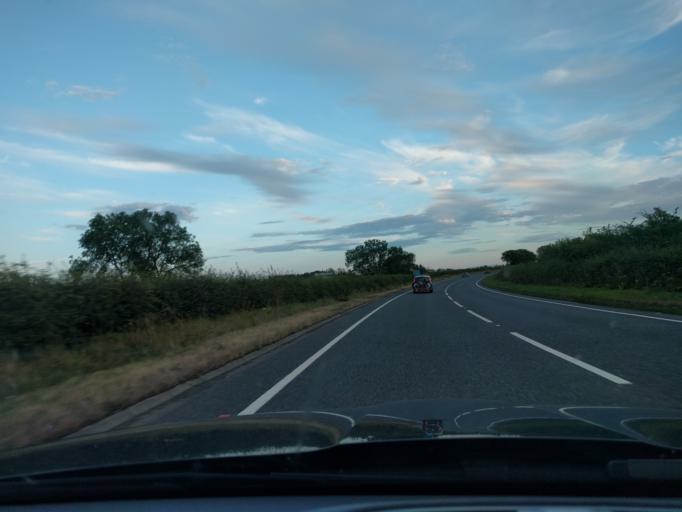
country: GB
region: England
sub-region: Northumberland
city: Felton
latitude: 55.2564
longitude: -1.7031
